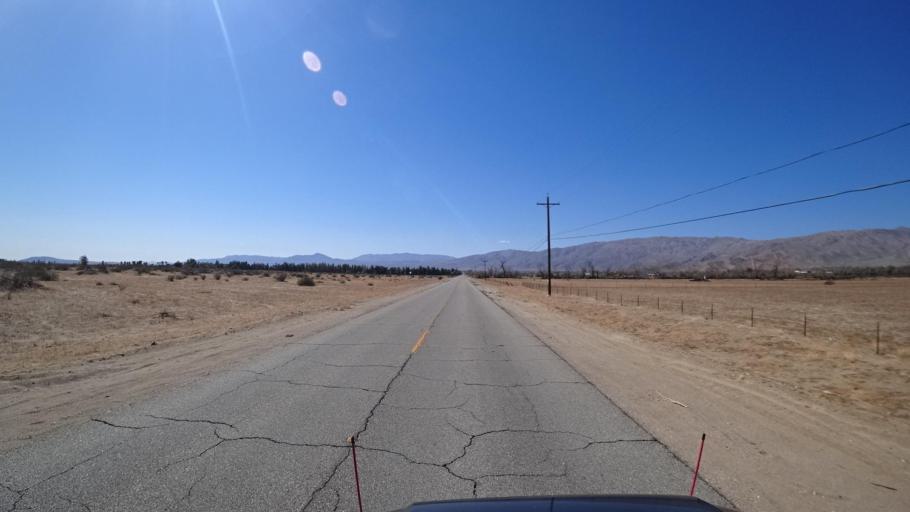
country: US
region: California
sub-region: San Diego County
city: Borrego Springs
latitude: 33.2766
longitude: -116.3663
